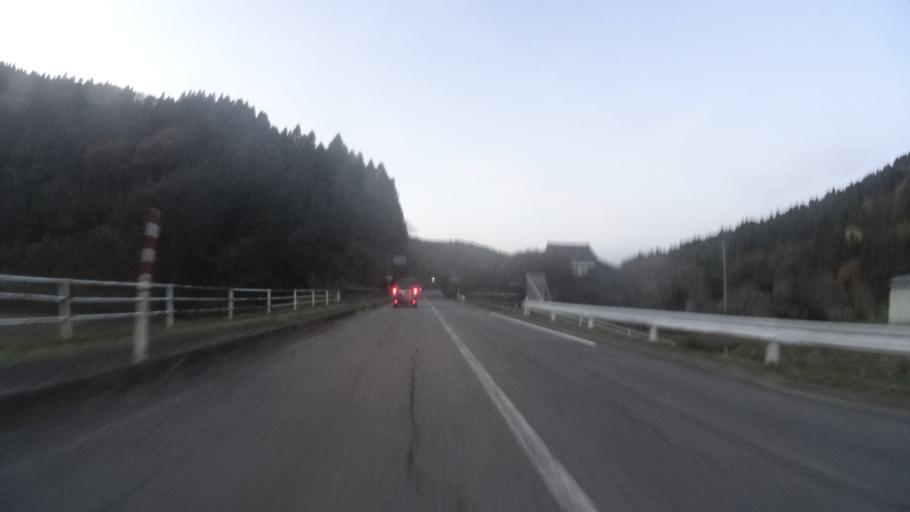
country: JP
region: Ishikawa
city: Nanao
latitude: 37.3577
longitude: 136.8666
